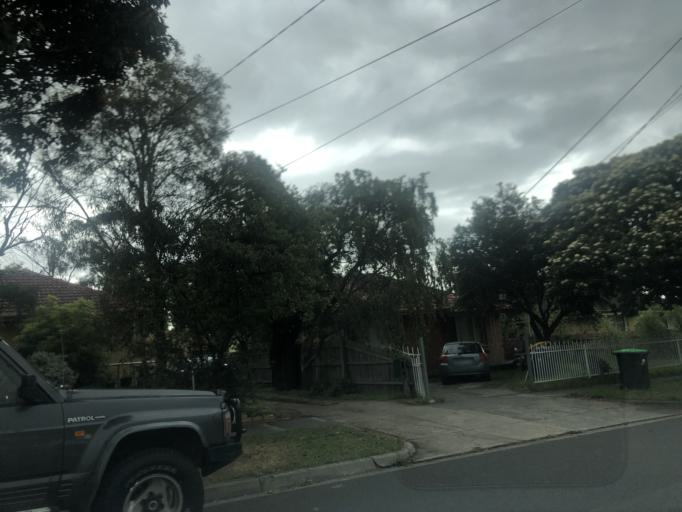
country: AU
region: Victoria
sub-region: Greater Dandenong
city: Dandenong North
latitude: -37.9726
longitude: 145.2215
